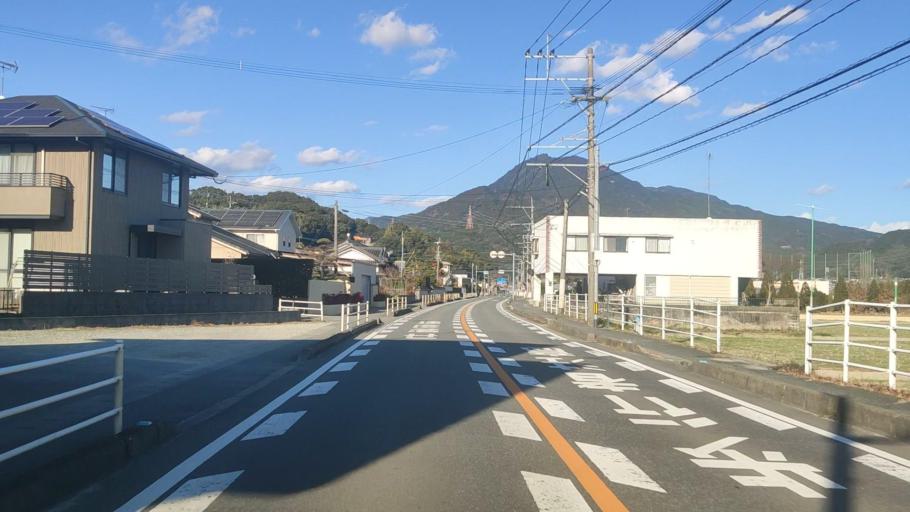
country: JP
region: Fukuoka
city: Dazaifu
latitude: 33.5003
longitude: 130.5494
